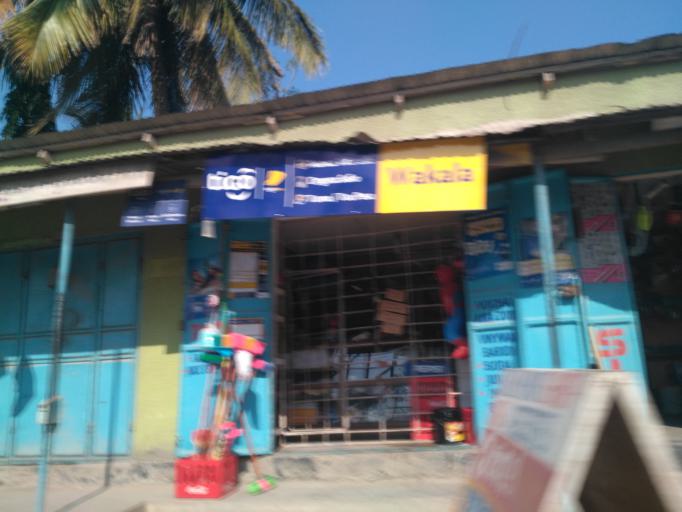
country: TZ
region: Dar es Salaam
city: Dar es Salaam
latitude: -6.8583
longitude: 39.3102
